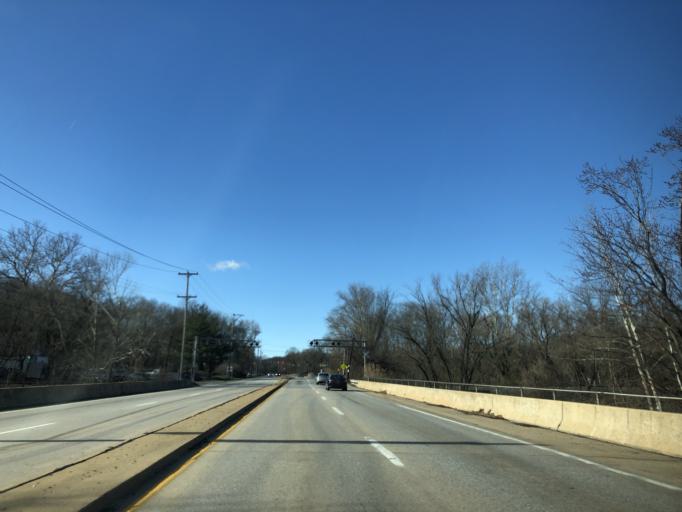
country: US
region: Pennsylvania
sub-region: Chester County
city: West Chester
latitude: 39.8718
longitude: -75.5955
